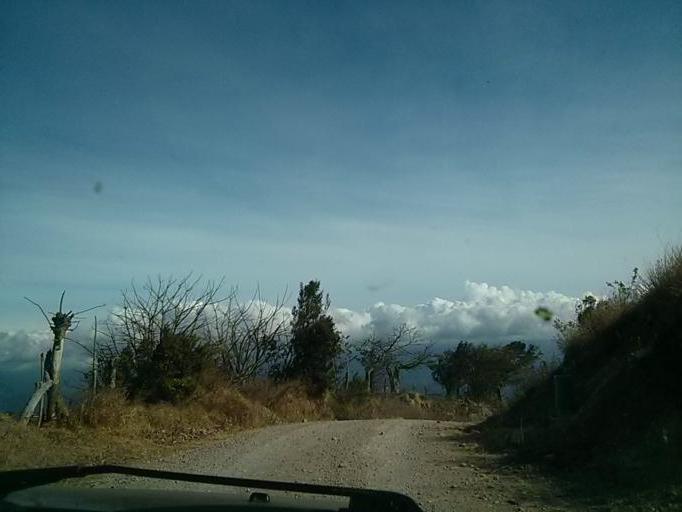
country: CR
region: Cartago
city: Cot
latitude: 9.9153
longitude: -83.9078
